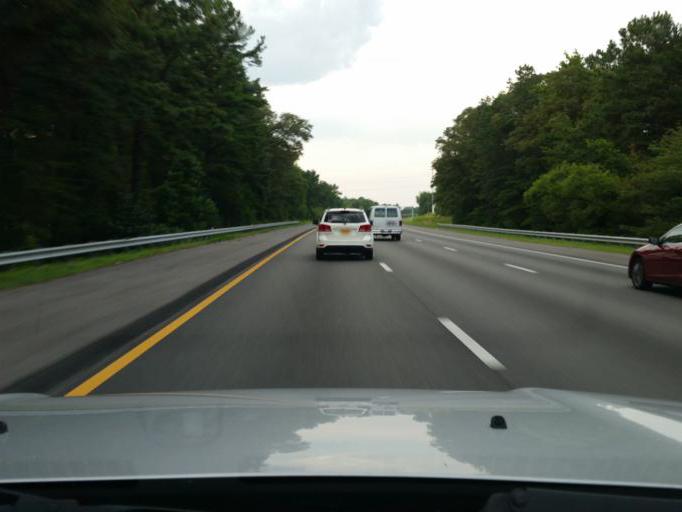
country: US
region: Virginia
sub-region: Caroline County
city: Bowling Green
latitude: 38.0111
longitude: -77.4980
